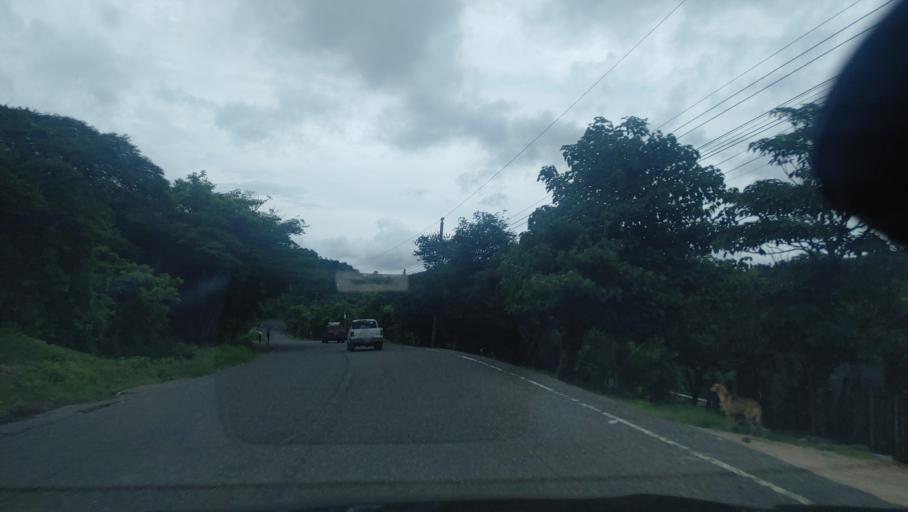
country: HN
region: Choluteca
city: San Marcos de Colon
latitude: 13.3766
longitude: -86.8876
